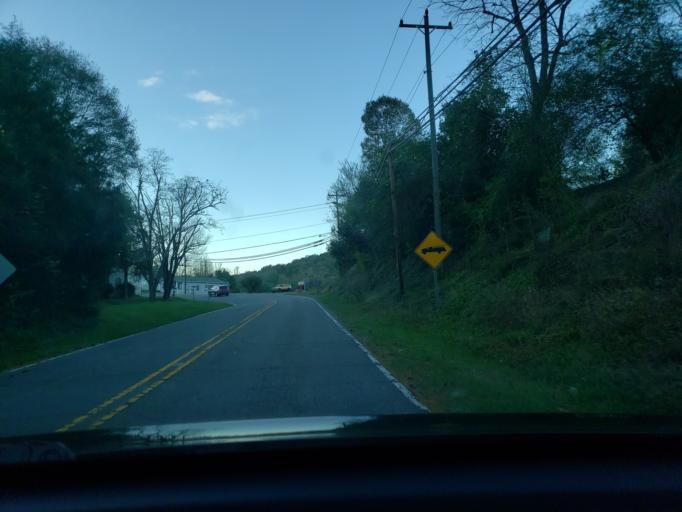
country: US
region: North Carolina
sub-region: Stokes County
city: Danbury
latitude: 36.4086
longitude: -80.2025
